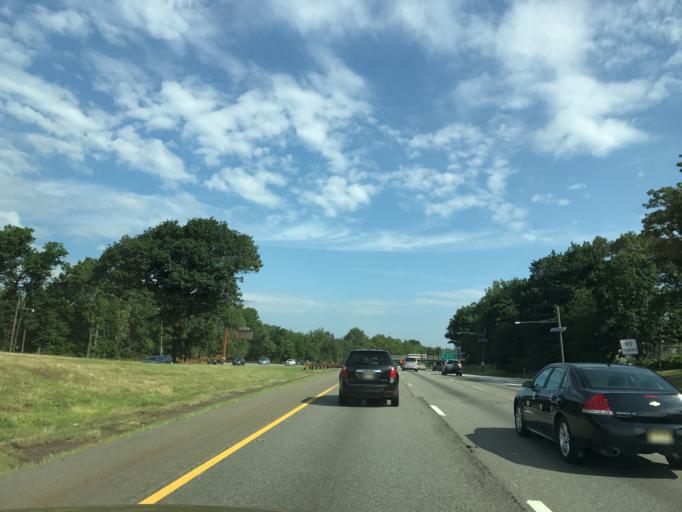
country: US
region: New Jersey
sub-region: Essex County
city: Brookdale
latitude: 40.8301
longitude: -74.1774
